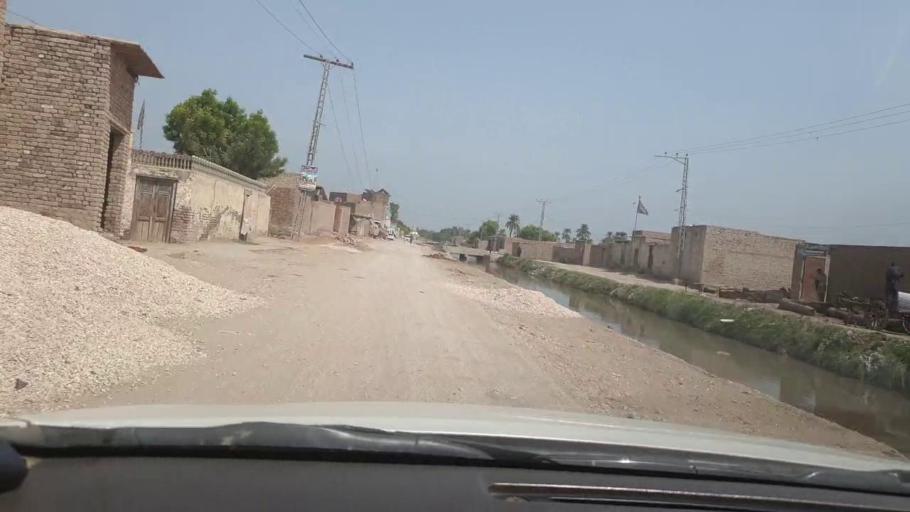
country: PK
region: Sindh
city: Shikarpur
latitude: 27.9447
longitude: 68.6334
